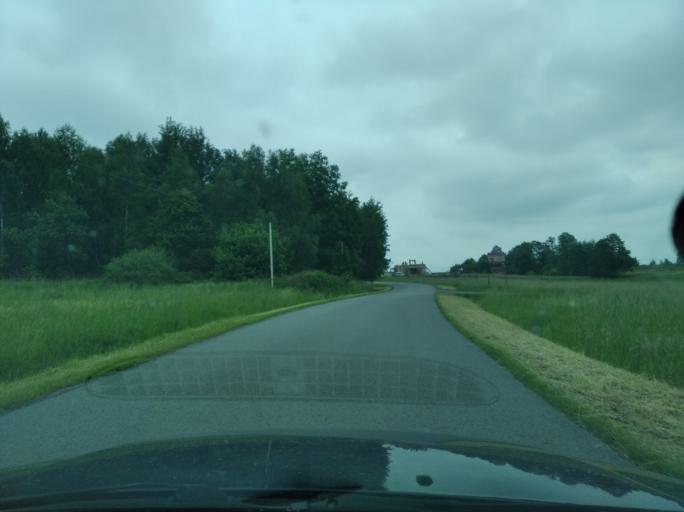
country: PL
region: Subcarpathian Voivodeship
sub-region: Powiat kolbuszowski
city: Niwiska
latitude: 50.2158
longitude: 21.6791
